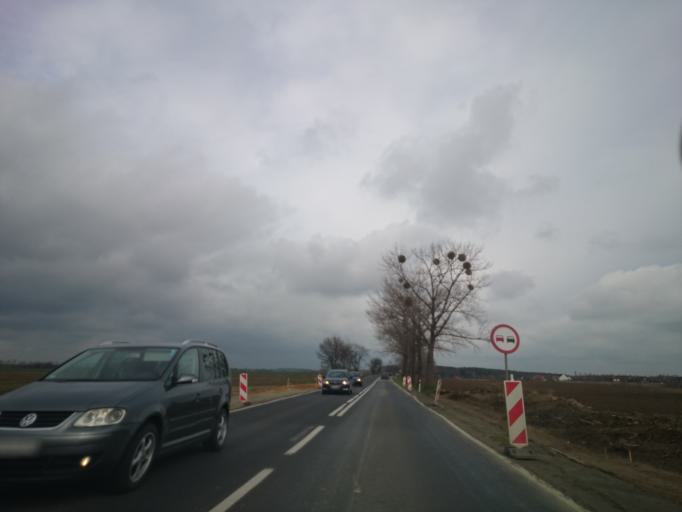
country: PL
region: Opole Voivodeship
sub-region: Powiat nyski
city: Nysa
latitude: 50.4757
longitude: 17.2635
